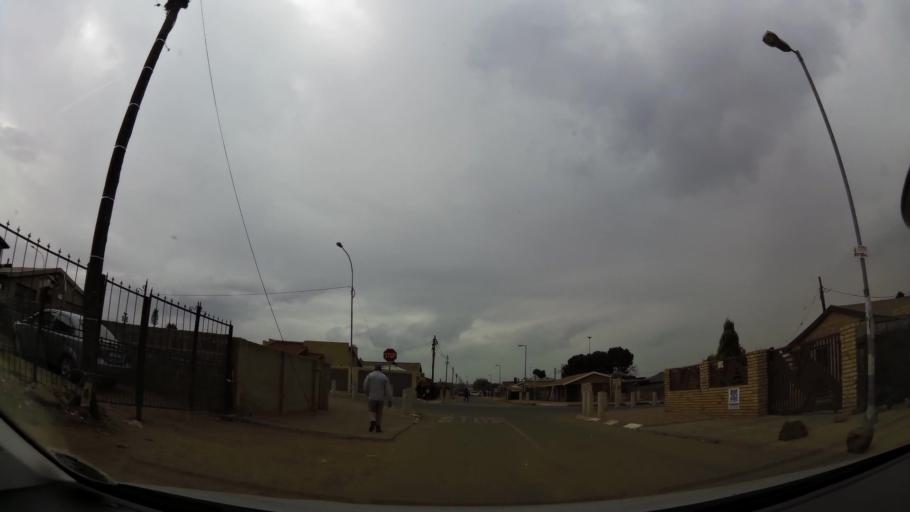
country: ZA
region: Gauteng
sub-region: City of Johannesburg Metropolitan Municipality
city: Soweto
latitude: -26.2596
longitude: 27.8653
